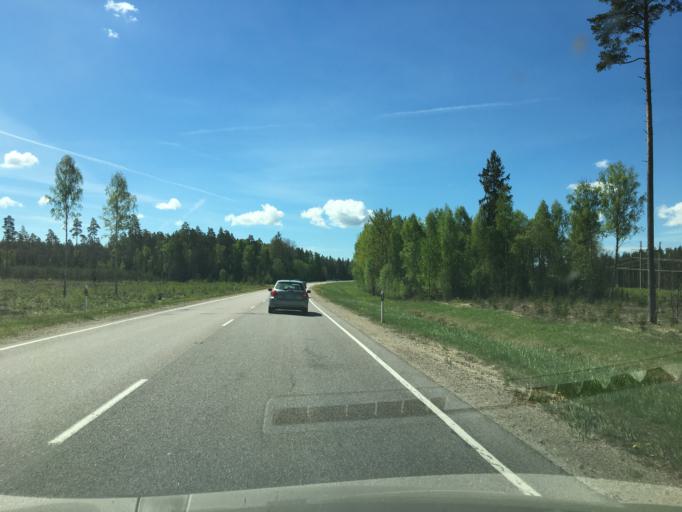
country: EE
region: Valgamaa
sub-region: Valga linn
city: Valga
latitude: 57.8871
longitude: 26.1652
